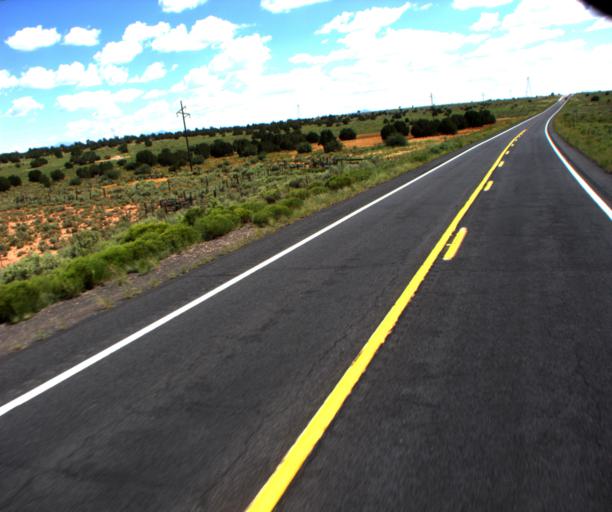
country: US
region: Arizona
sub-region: Coconino County
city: Grand Canyon Village
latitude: 35.7778
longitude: -112.1293
